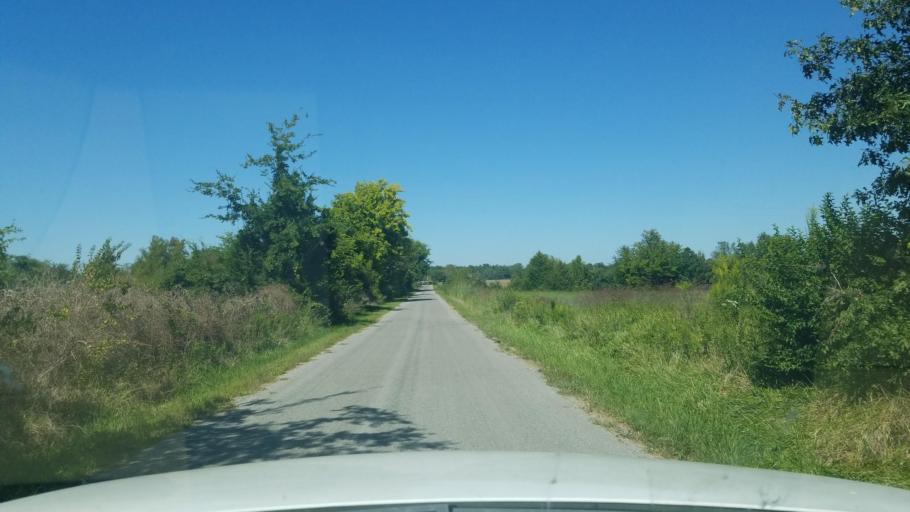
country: US
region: Illinois
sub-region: Saline County
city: Eldorado
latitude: 37.8583
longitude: -88.5119
